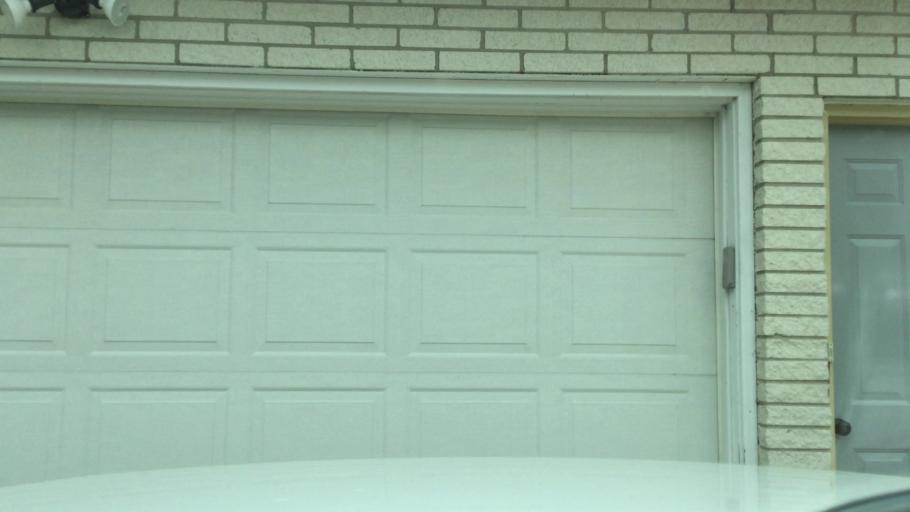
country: US
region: Michigan
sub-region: Genesee County
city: Flushing
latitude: 43.0251
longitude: -83.7994
